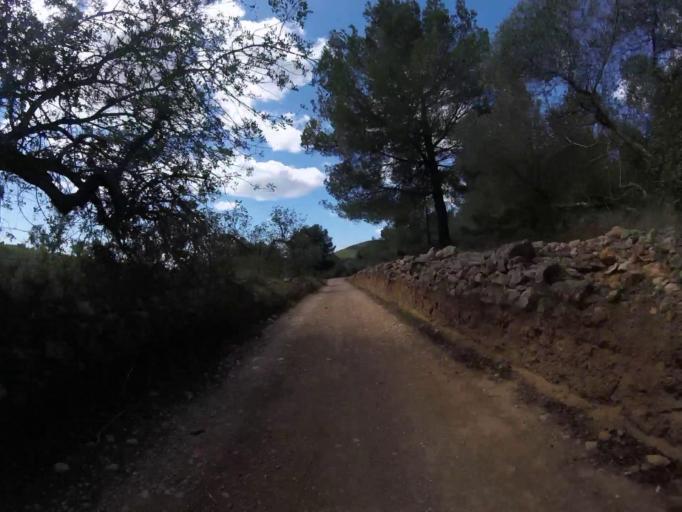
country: ES
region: Valencia
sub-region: Provincia de Castello
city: Santa Magdalena de Pulpis
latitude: 40.3217
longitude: 0.3331
